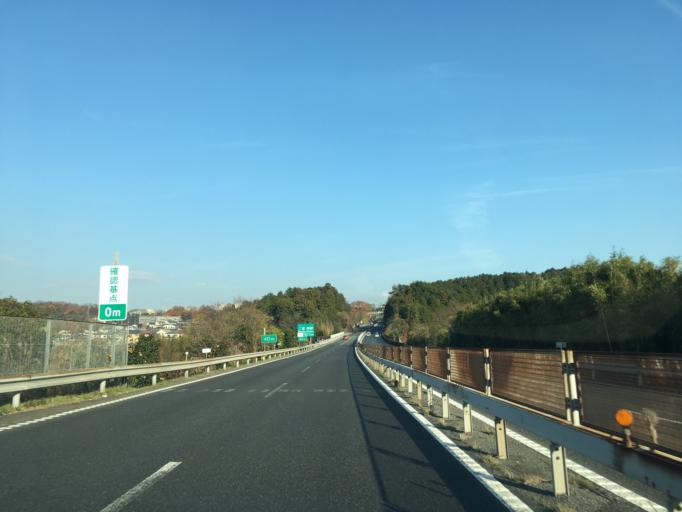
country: JP
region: Kanagawa
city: Ninomiya
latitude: 35.3061
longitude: 139.2275
